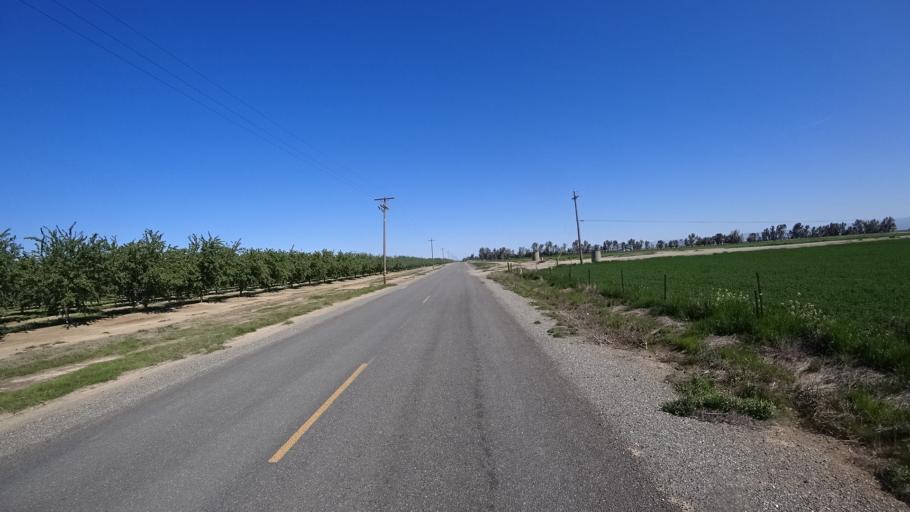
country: US
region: California
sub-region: Glenn County
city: Hamilton City
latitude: 39.6809
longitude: -122.1033
